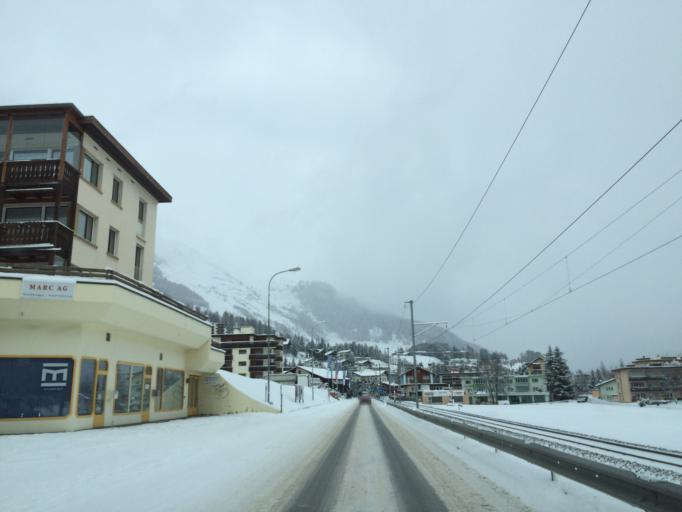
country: CH
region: Grisons
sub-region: Praettigau/Davos District
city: Davos
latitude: 46.8037
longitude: 9.8379
